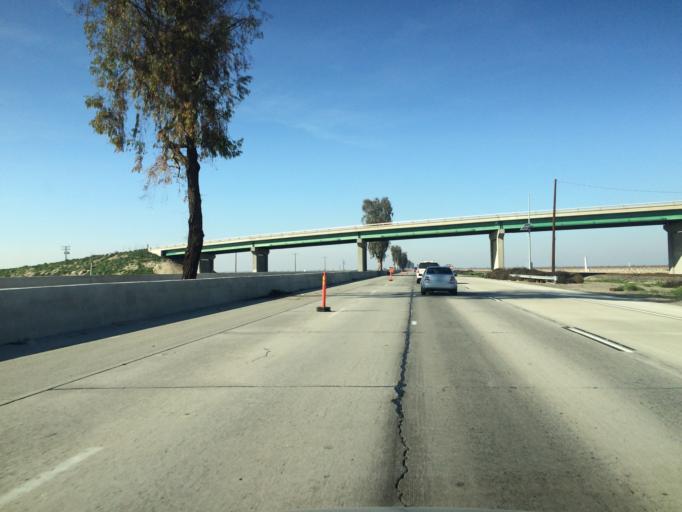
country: US
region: California
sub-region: Tulare County
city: Goshen
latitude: 36.3842
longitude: -119.4431
